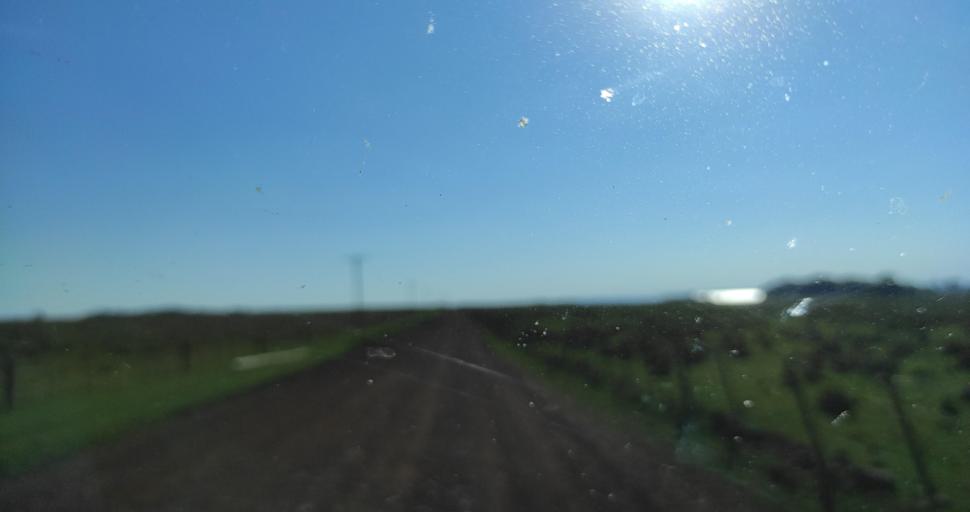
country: PY
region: Itapua
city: Carmen del Parana
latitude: -27.4101
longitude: -56.1537
